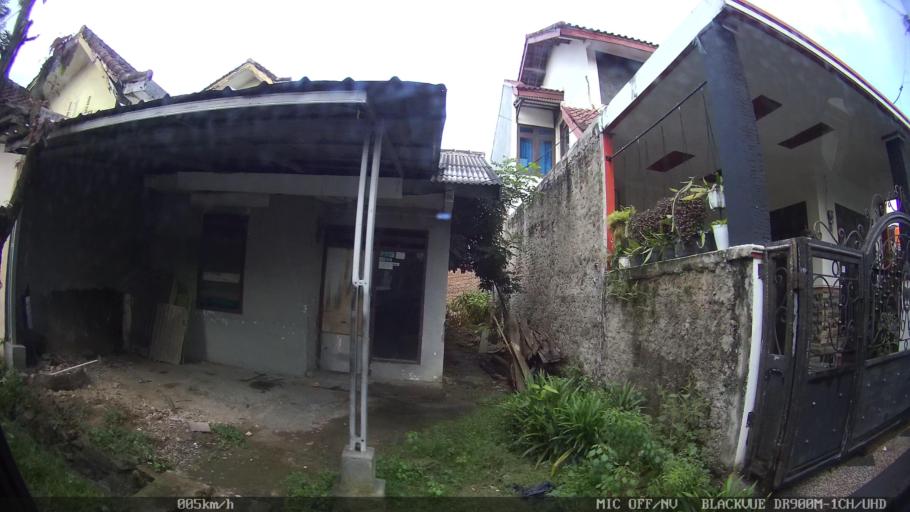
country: ID
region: Lampung
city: Kedaton
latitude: -5.3896
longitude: 105.3022
